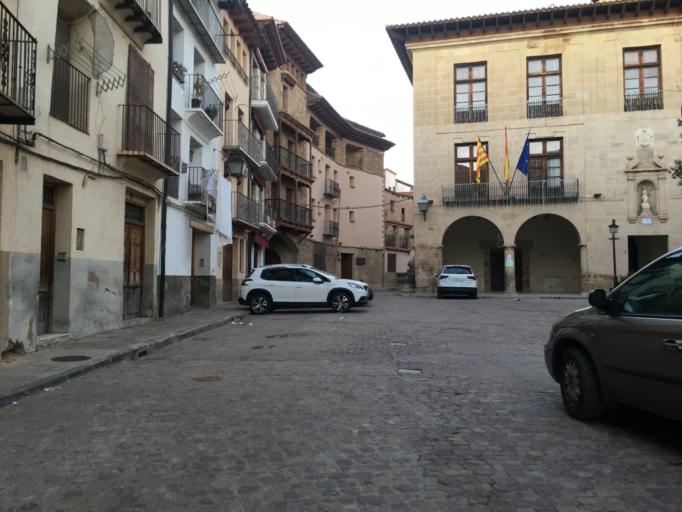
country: ES
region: Aragon
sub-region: Provincia de Teruel
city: Mora de Rubielos
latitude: 40.2514
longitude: -0.7532
